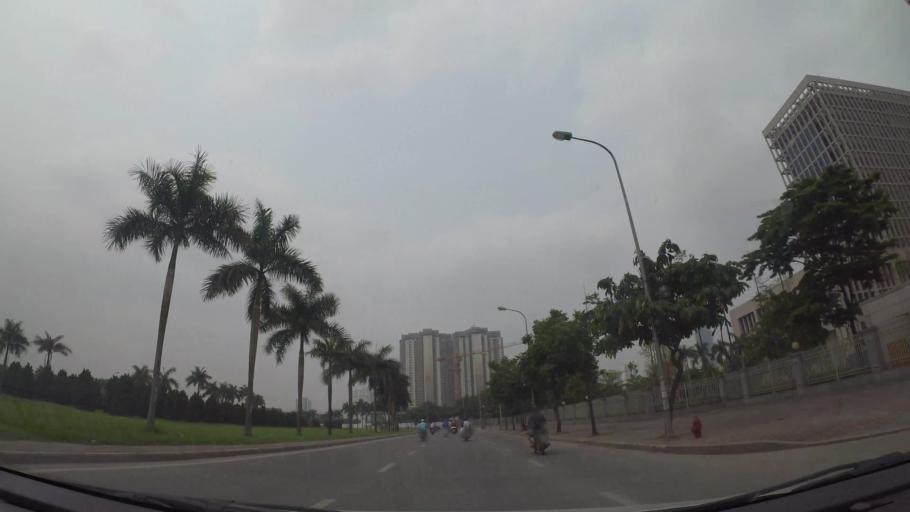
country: VN
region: Ha Noi
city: Thanh Xuan
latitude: 21.0067
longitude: 105.7742
